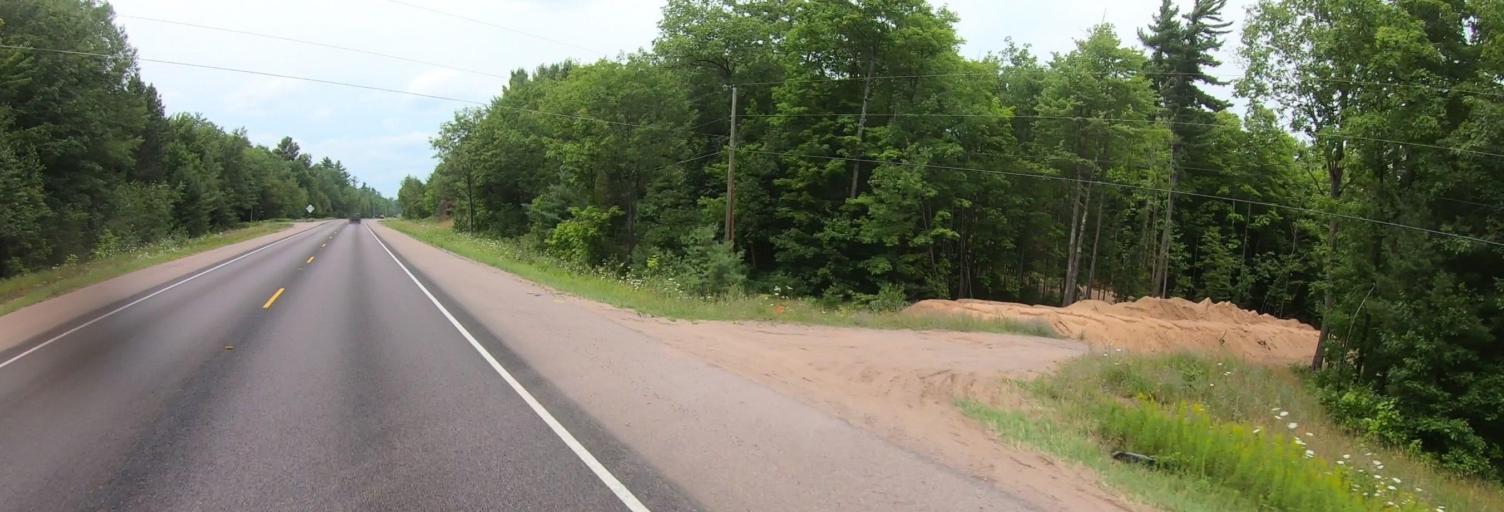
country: US
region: Michigan
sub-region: Marquette County
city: Marquette
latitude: 46.4685
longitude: -87.4366
